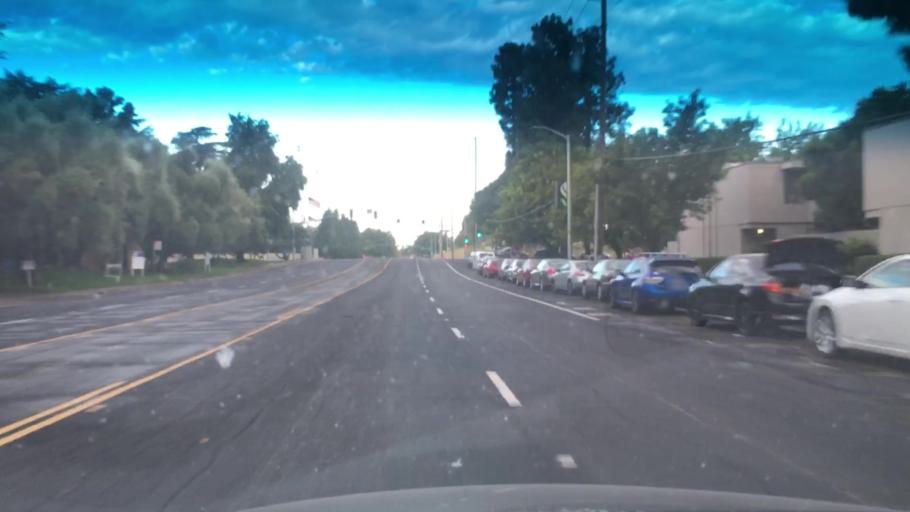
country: US
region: California
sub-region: Sacramento County
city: Rosemont
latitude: 38.5543
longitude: -121.4138
